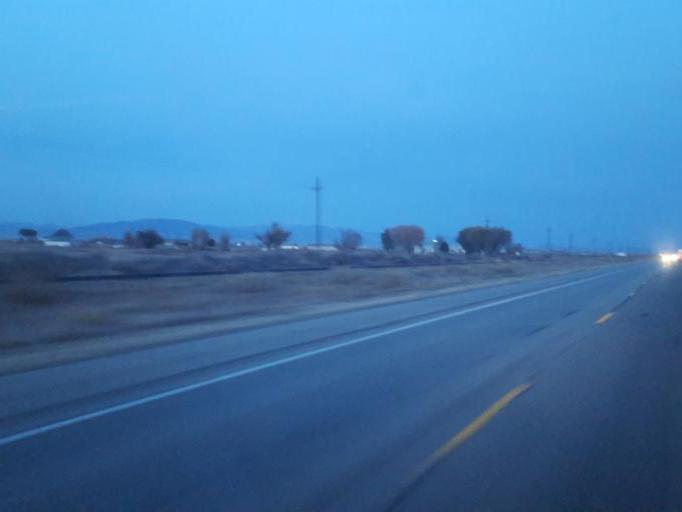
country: US
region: Colorado
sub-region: Alamosa County
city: Alamosa
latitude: 37.5001
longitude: -105.9533
